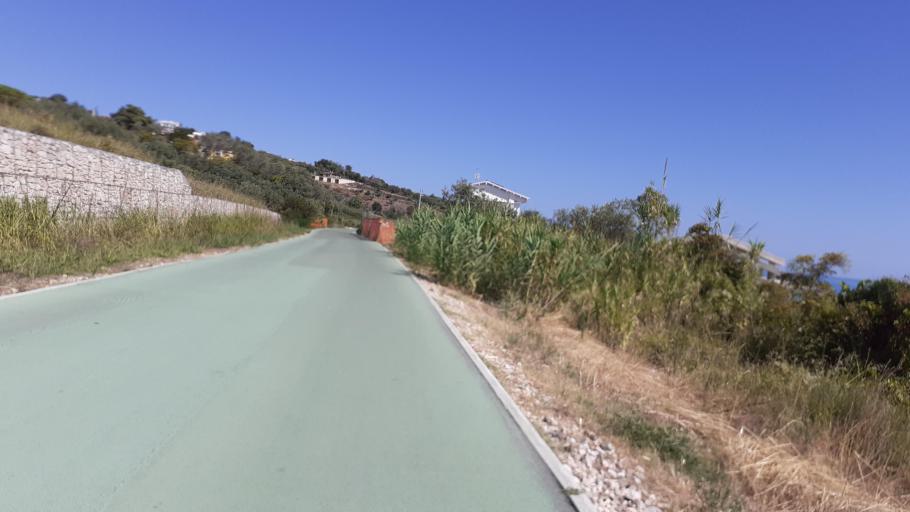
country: IT
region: Abruzzo
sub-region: Provincia di Chieti
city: Vasto
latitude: 42.1168
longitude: 14.7199
